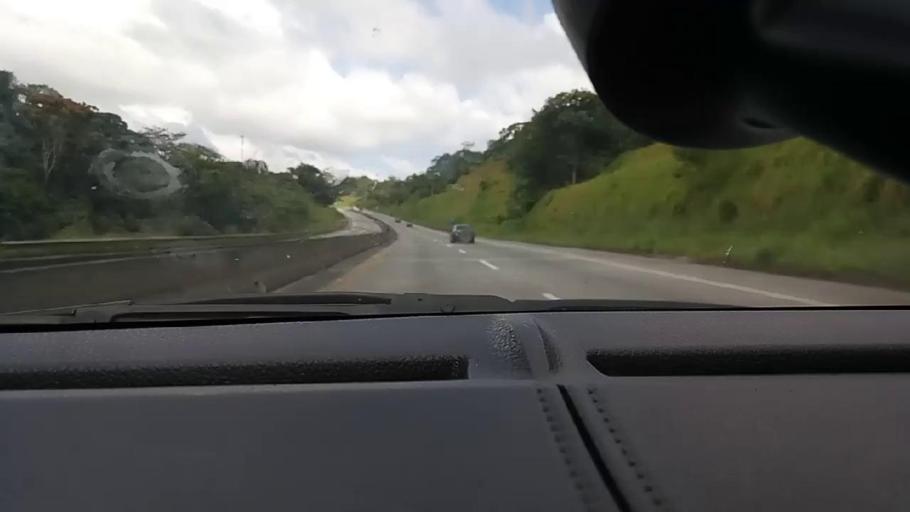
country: PA
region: Colon
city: Gatun
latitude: 9.2881
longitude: -79.7795
